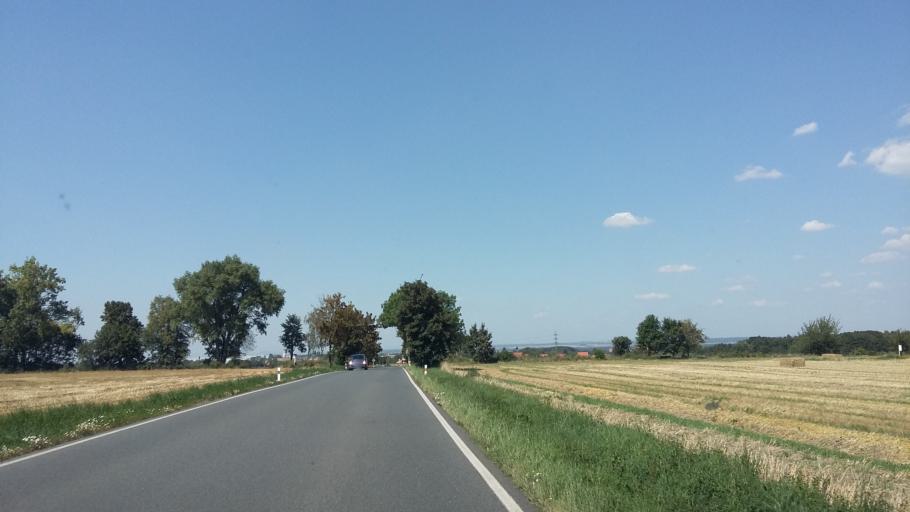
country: CZ
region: Central Bohemia
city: Zelenec
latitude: 50.1537
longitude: 14.6863
